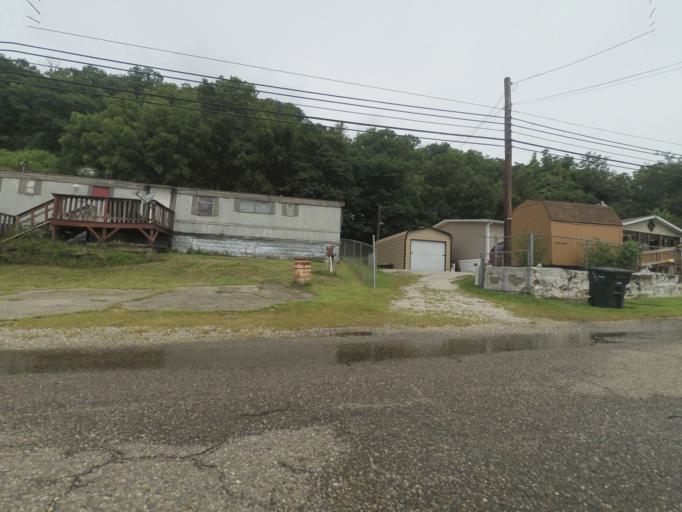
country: US
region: West Virginia
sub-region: Cabell County
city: Huntington
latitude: 38.4355
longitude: -82.4201
